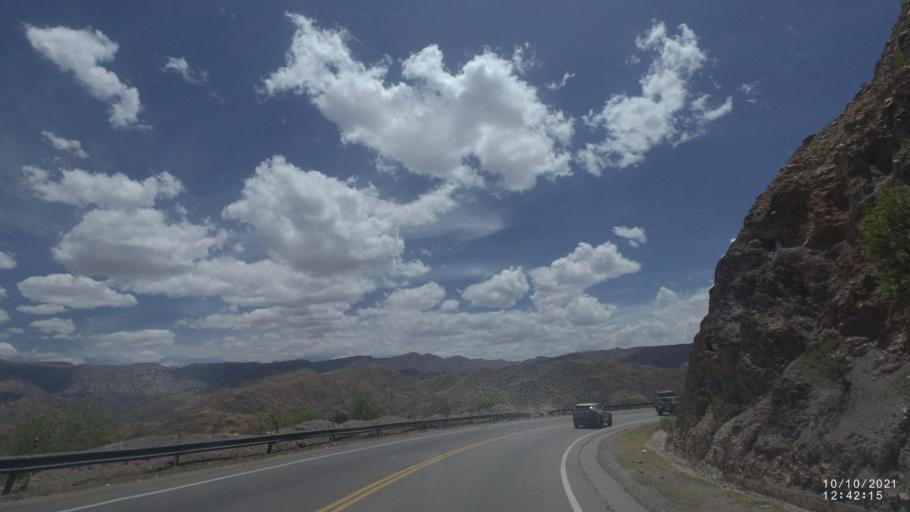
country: BO
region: Cochabamba
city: Irpa Irpa
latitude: -17.6308
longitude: -66.3917
